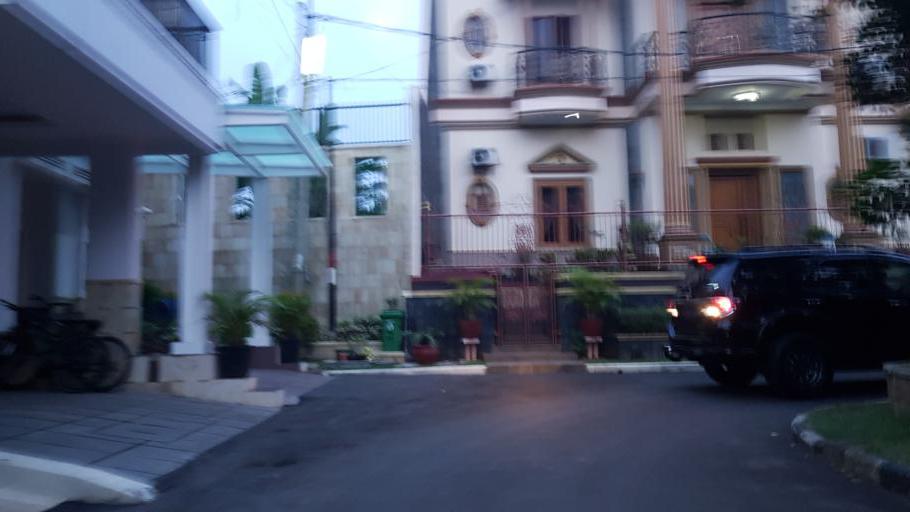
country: ID
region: West Java
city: Pamulang
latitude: -6.3322
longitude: 106.7963
